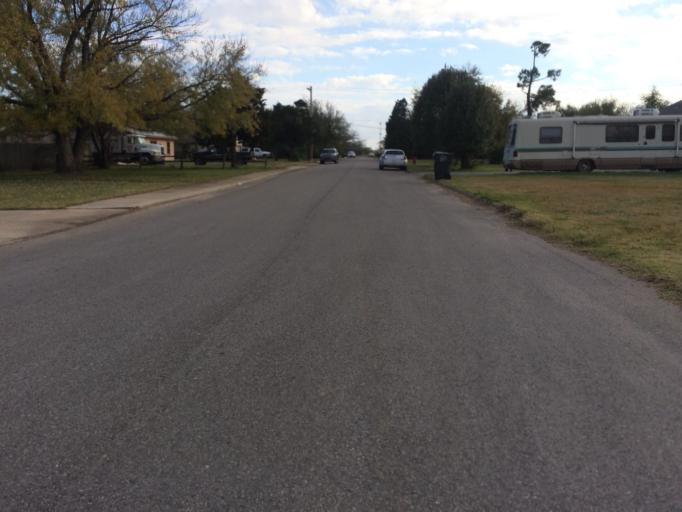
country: US
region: Oklahoma
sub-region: Cleveland County
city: Norman
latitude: 35.2358
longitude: -97.4515
